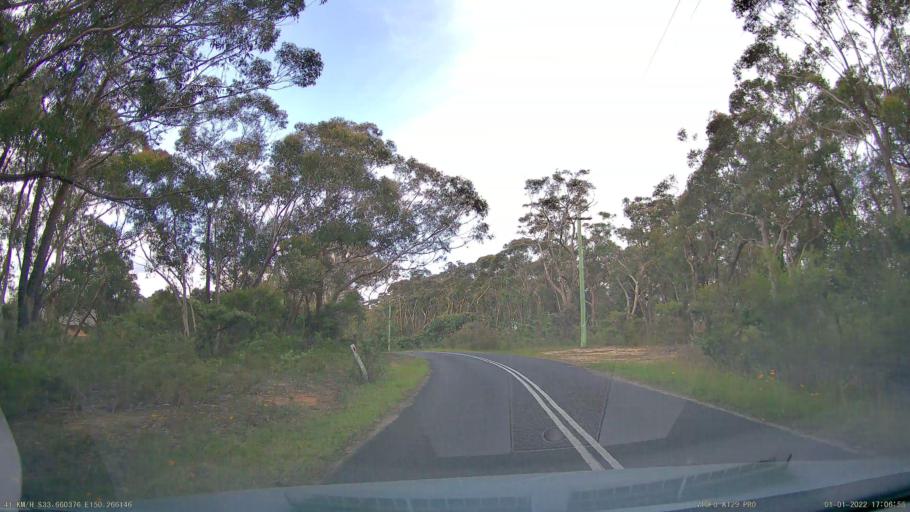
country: AU
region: New South Wales
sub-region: Blue Mountains Municipality
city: Blackheath
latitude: -33.6603
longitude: 150.2661
